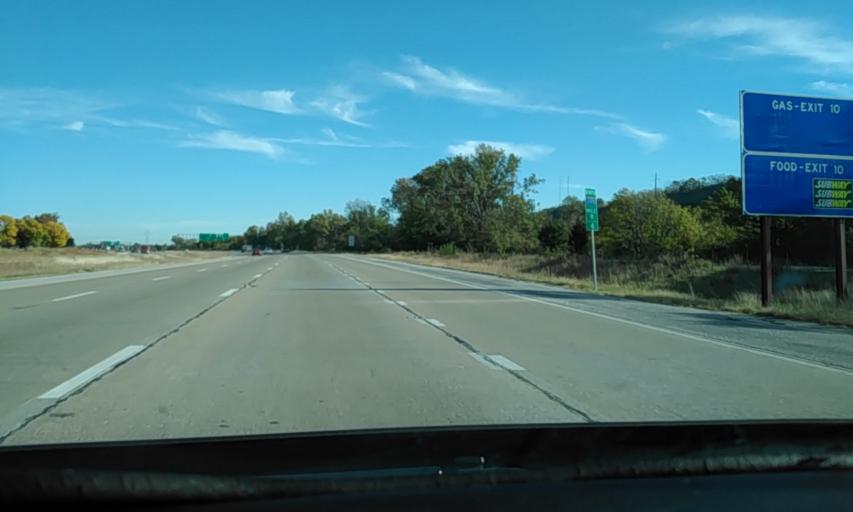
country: US
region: Illinois
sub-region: Saint Clair County
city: Dupo
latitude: 38.5121
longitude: -90.2023
